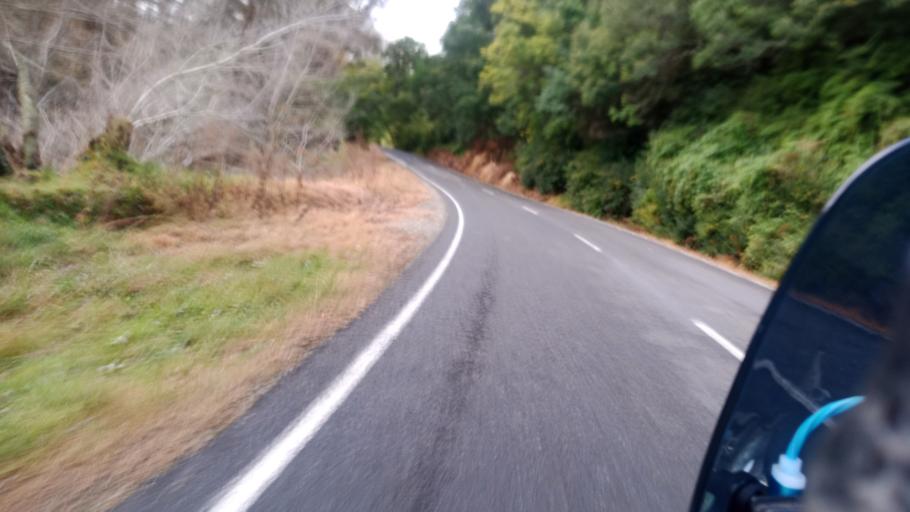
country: NZ
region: Gisborne
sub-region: Gisborne District
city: Gisborne
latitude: -38.4384
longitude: 177.8790
